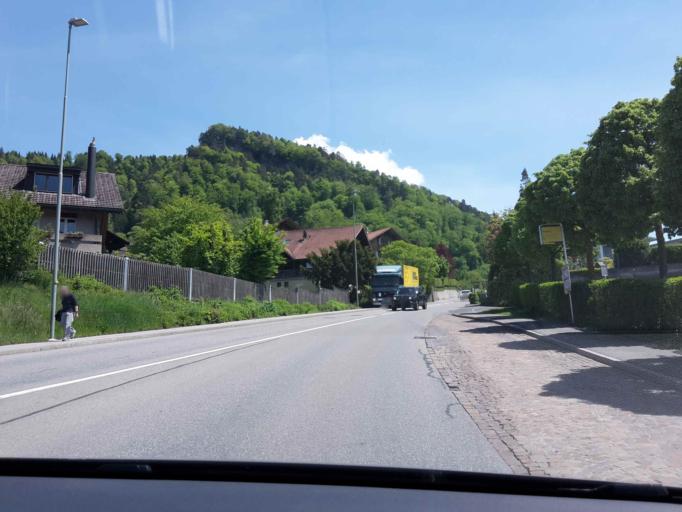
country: CH
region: Bern
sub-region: Thun District
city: Steffisburg
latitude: 46.7635
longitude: 7.6336
